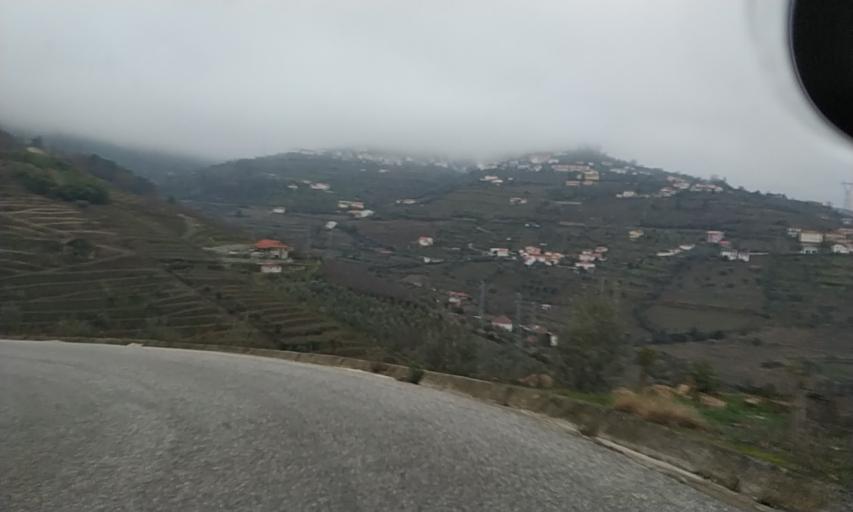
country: PT
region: Viseu
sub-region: Lamego
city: Lamego
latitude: 41.1186
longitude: -7.8030
